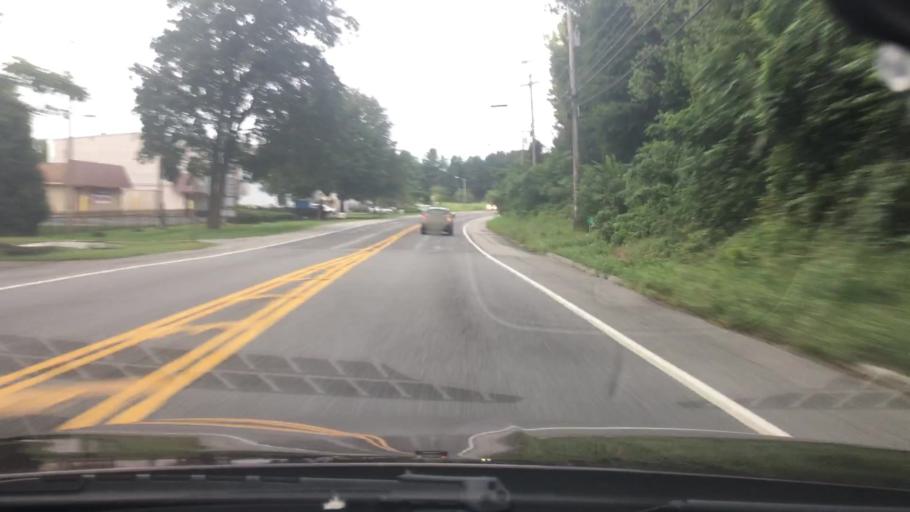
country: US
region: New York
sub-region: Dutchess County
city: Pleasant Valley
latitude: 41.7274
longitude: -73.8409
